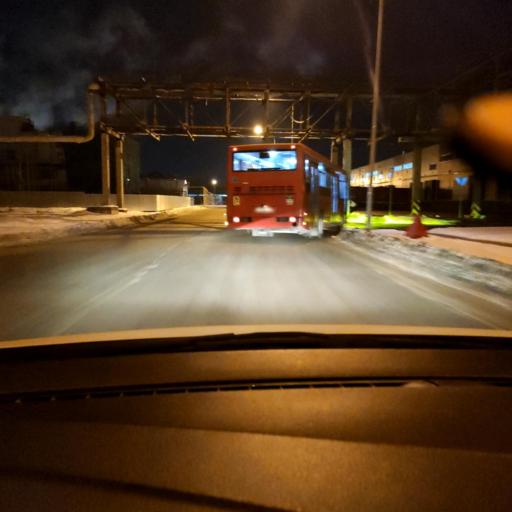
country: RU
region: Tatarstan
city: Staroye Arakchino
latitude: 55.8305
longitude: 49.0432
